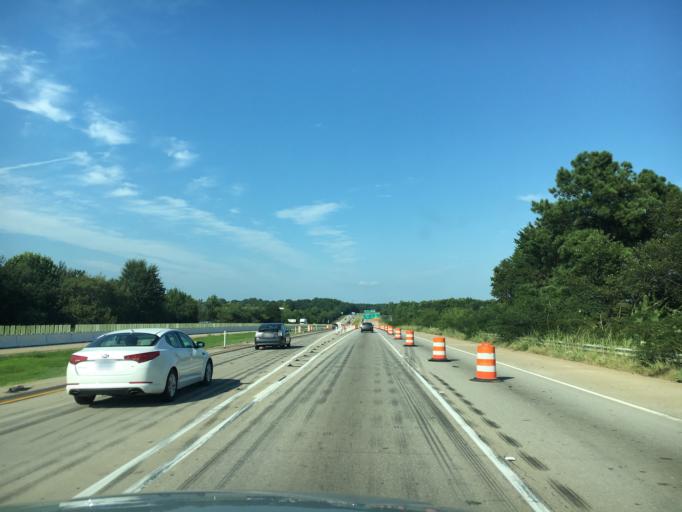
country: US
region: South Carolina
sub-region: Spartanburg County
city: Fairforest
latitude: 34.9679
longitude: -82.0280
